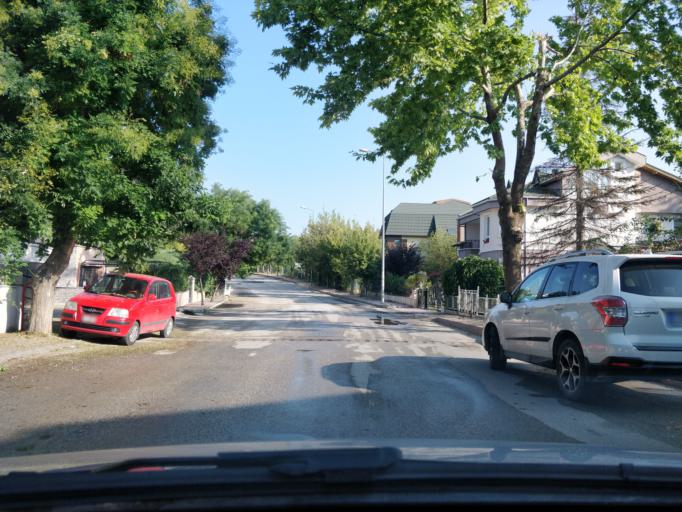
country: TR
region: Ankara
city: Batikent
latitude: 39.8956
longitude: 32.7263
